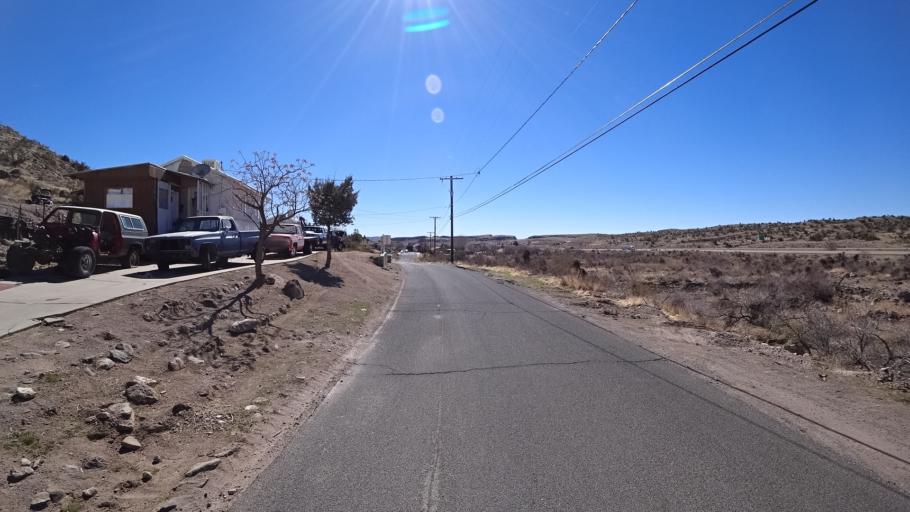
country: US
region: Arizona
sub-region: Mohave County
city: Kingman
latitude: 35.2003
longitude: -114.0643
